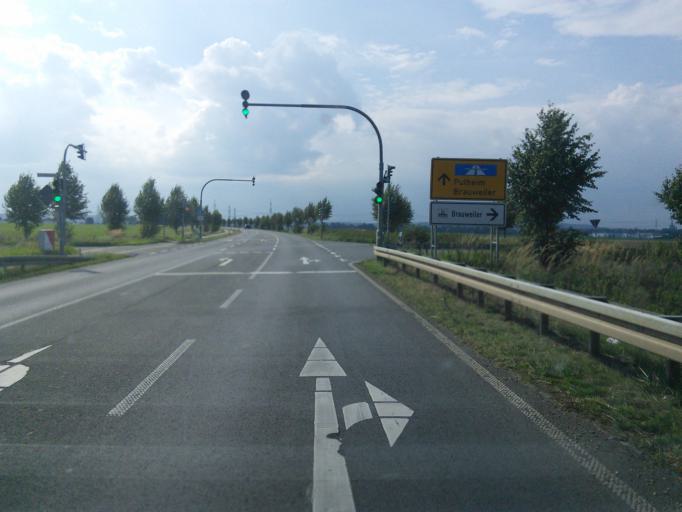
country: DE
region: North Rhine-Westphalia
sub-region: Regierungsbezirk Koln
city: Frechen
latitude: 50.9569
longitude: 6.8243
